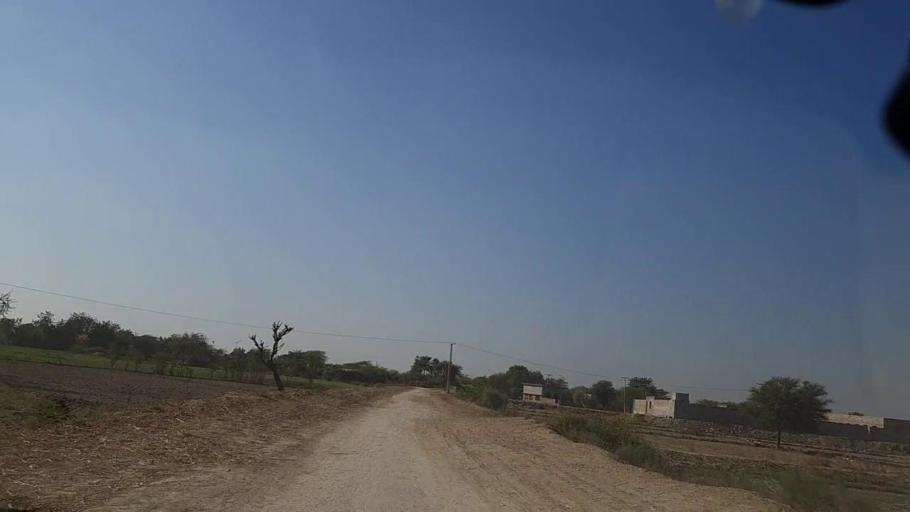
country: PK
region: Sindh
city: Mirpur Khas
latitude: 25.5197
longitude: 68.9273
